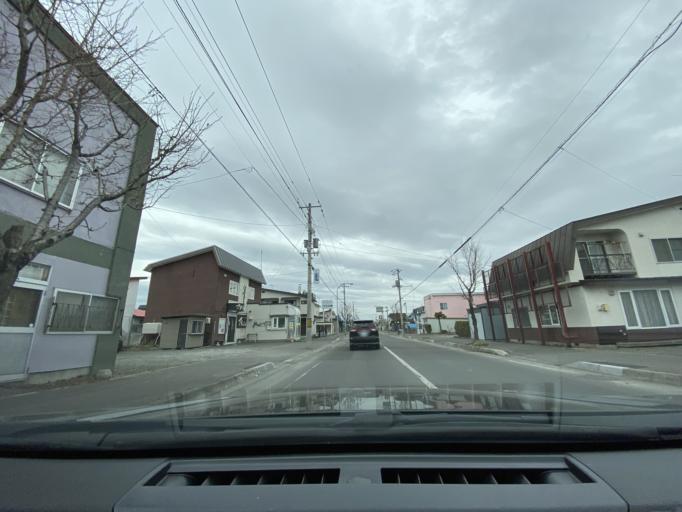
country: JP
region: Hokkaido
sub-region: Asahikawa-shi
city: Asahikawa
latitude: 43.7930
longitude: 142.4173
